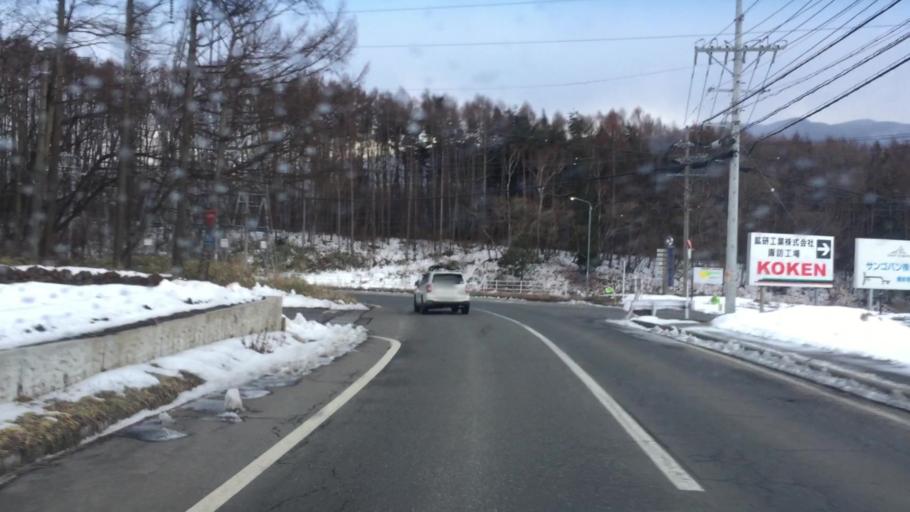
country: JP
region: Nagano
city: Chino
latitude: 35.9517
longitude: 138.2135
